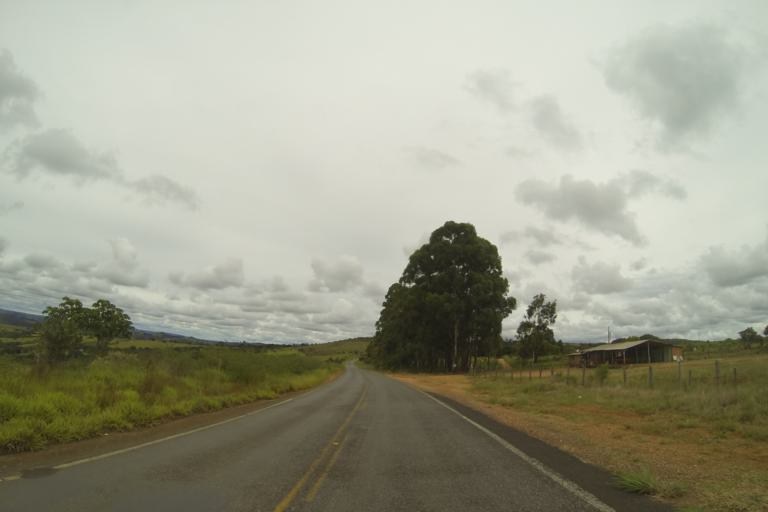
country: BR
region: Minas Gerais
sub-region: Ibia
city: Ibia
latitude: -19.6629
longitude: -46.4459
